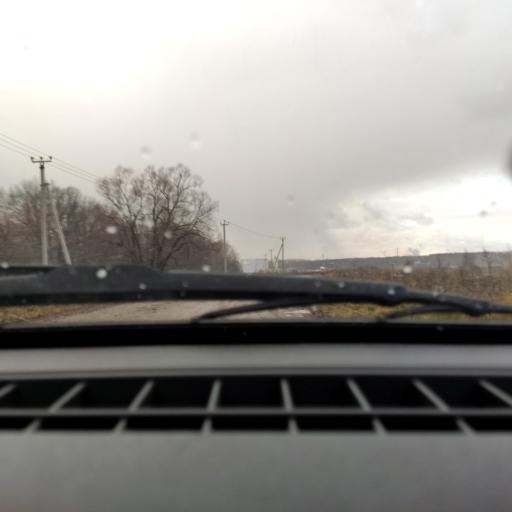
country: RU
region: Bashkortostan
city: Iglino
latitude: 54.7399
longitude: 56.3240
